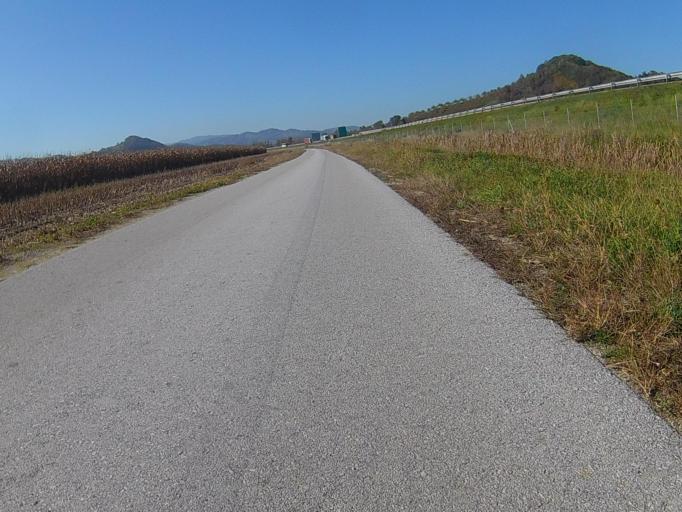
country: SI
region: Pesnica
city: Pesnica pri Mariboru
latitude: 46.5925
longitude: 15.7062
